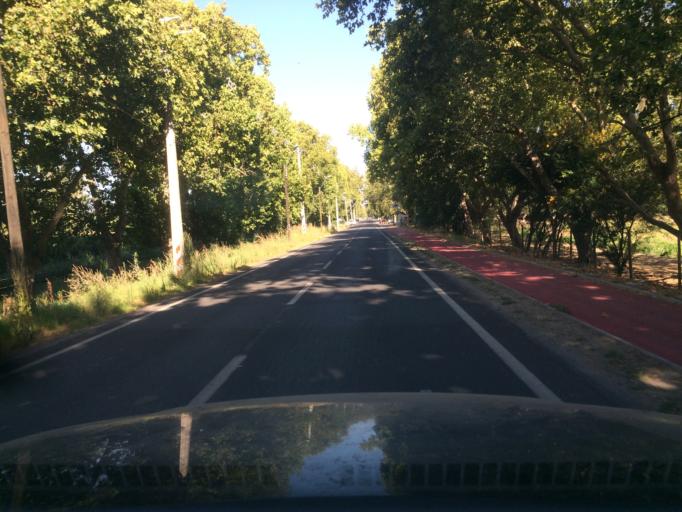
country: CL
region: Santiago Metropolitan
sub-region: Provincia de Melipilla
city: Melipilla
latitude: -33.4904
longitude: -71.1752
